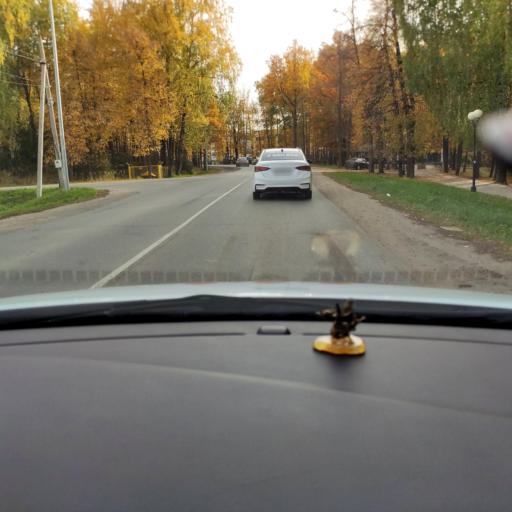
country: RU
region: Tatarstan
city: Vysokaya Gora
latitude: 55.9265
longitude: 49.3035
